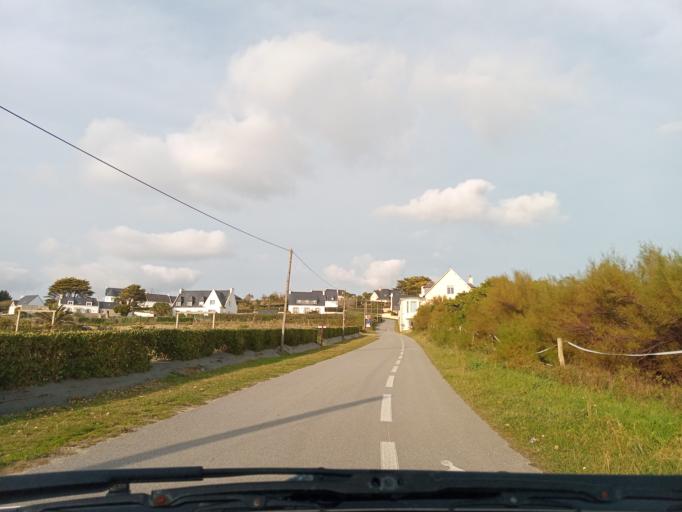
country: FR
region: Brittany
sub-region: Departement du Finistere
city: Plouhinec
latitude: 48.0030
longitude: -4.5005
